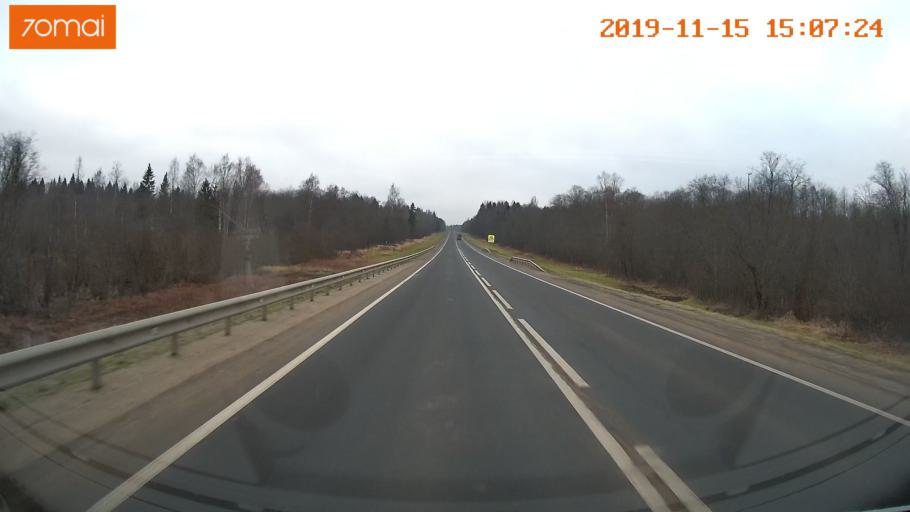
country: RU
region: Jaroslavl
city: Prechistoye
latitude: 58.3840
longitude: 40.2964
